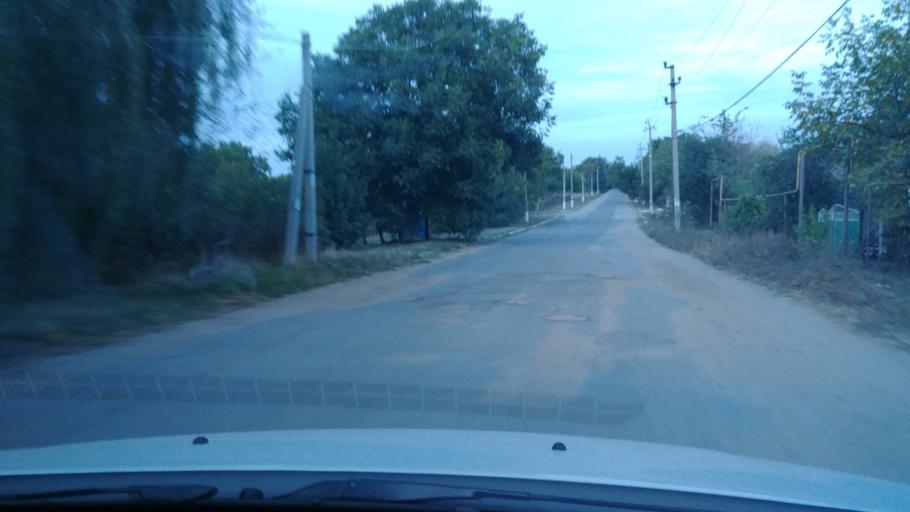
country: MD
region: Rezina
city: Saharna
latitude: 47.6758
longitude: 28.9599
